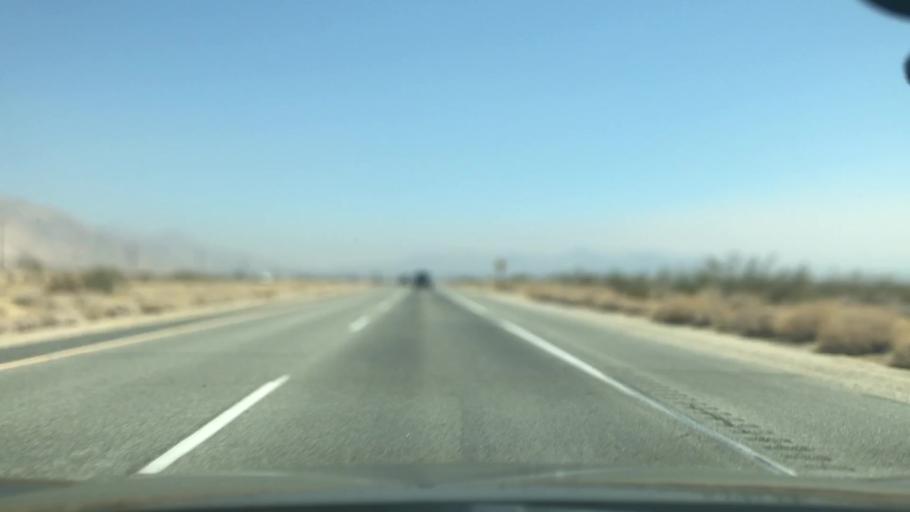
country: US
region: California
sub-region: Kern County
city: Inyokern
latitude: 35.7374
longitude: -117.8694
